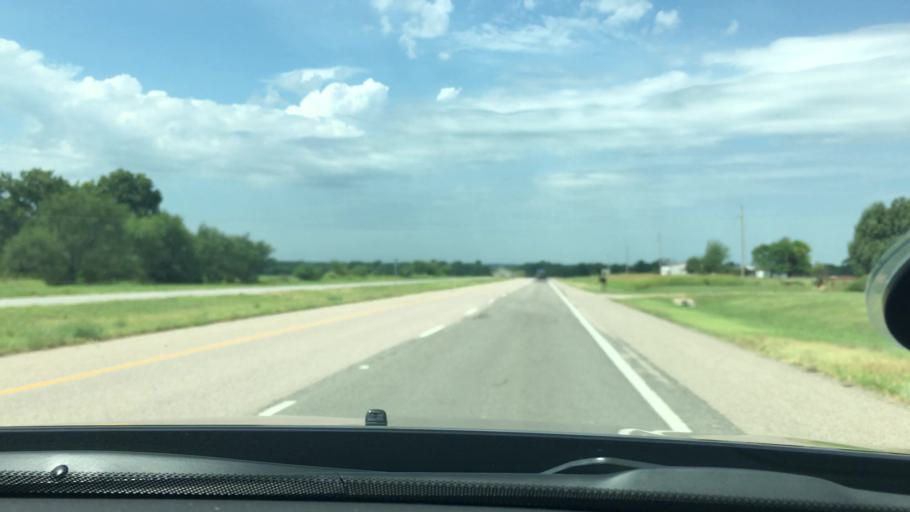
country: US
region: Oklahoma
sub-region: Pontotoc County
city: Ada
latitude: 34.6744
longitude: -96.7765
